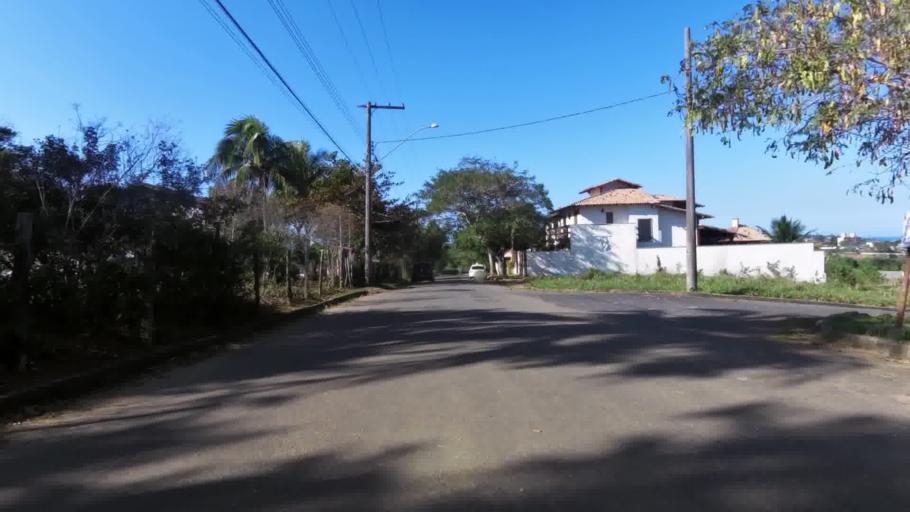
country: BR
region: Espirito Santo
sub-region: Guarapari
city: Guarapari
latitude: -20.7363
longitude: -40.5548
